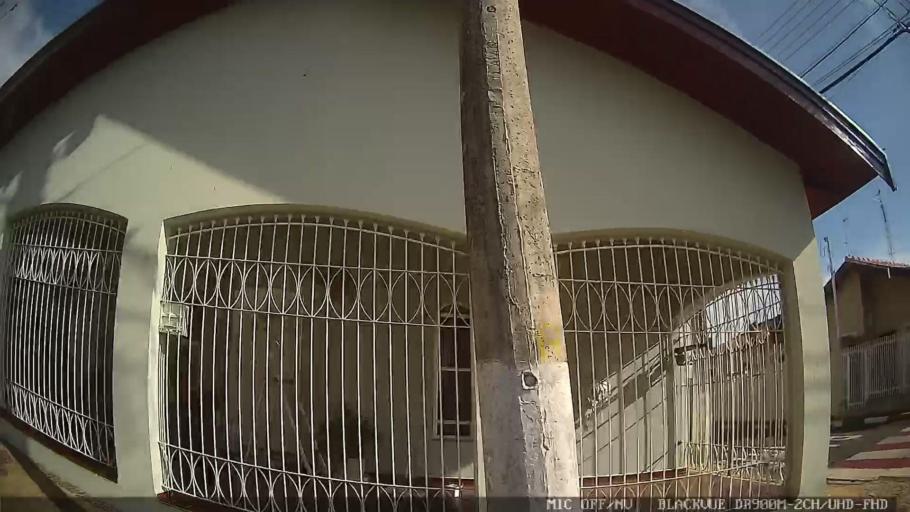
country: BR
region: Sao Paulo
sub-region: Laranjal Paulista
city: Laranjal Paulista
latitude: -23.0841
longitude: -47.7889
